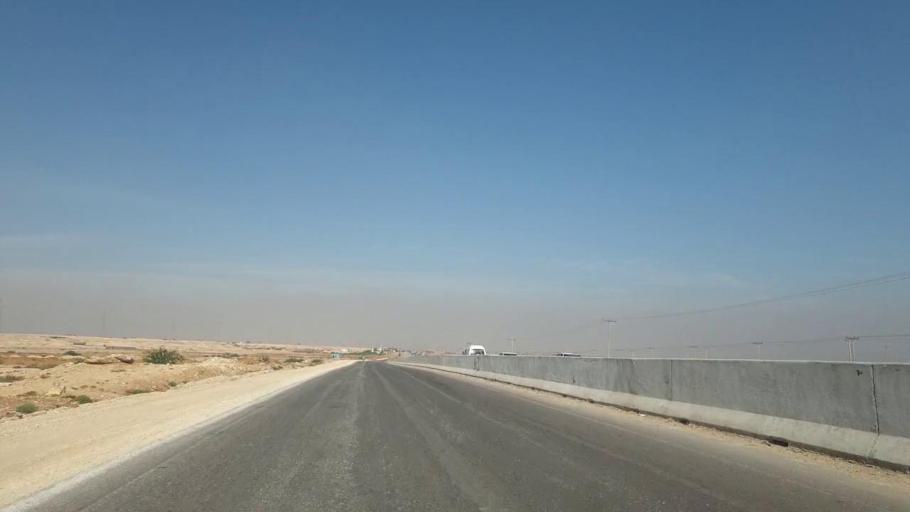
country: PK
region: Sindh
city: Jamshoro
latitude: 25.4891
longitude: 68.2720
